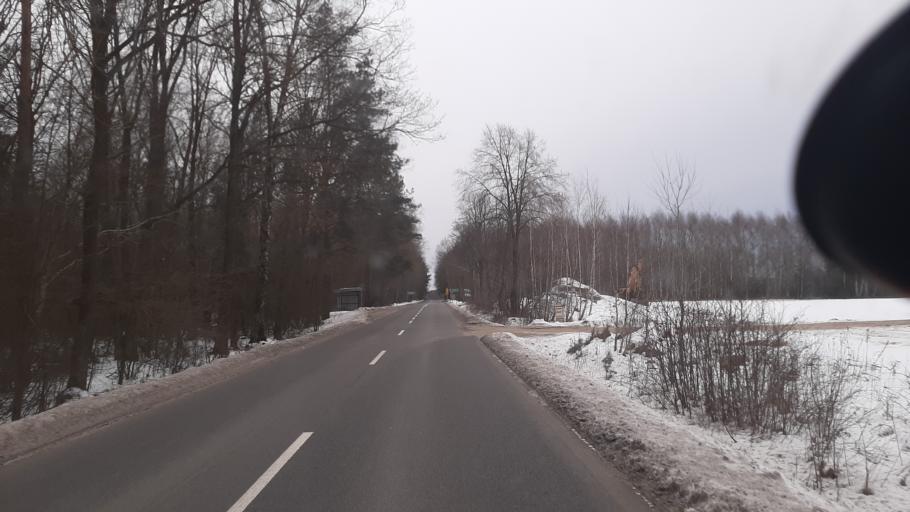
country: PL
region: Lublin Voivodeship
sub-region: Powiat lubartowski
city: Kamionka
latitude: 51.4993
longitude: 22.4068
